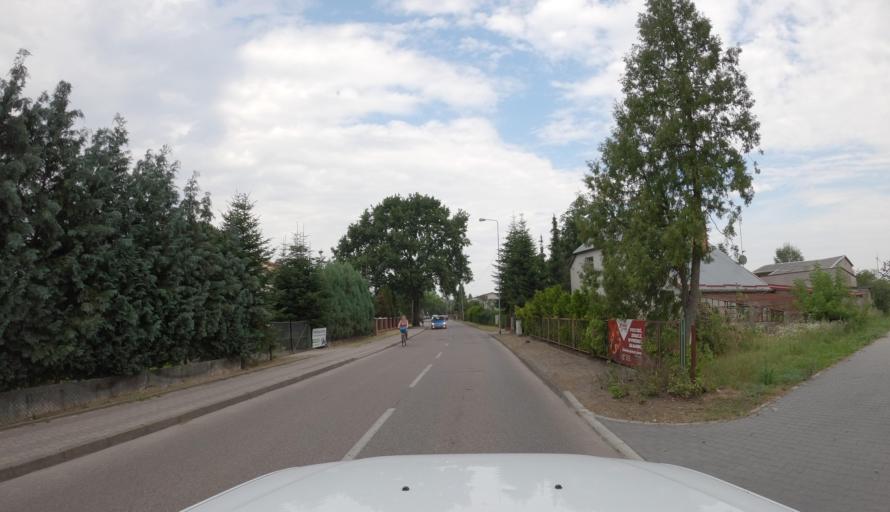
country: PL
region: West Pomeranian Voivodeship
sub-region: Powiat bialogardzki
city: Bialogard
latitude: 54.0088
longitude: 15.9965
